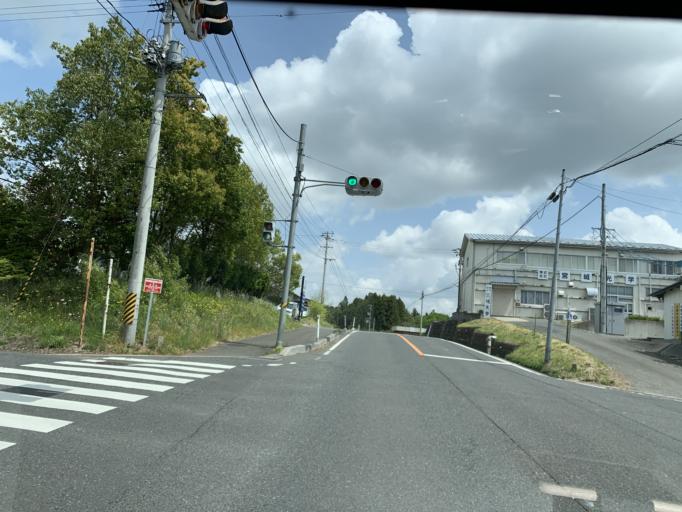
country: JP
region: Miyagi
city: Kogota
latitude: 38.6583
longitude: 141.0610
